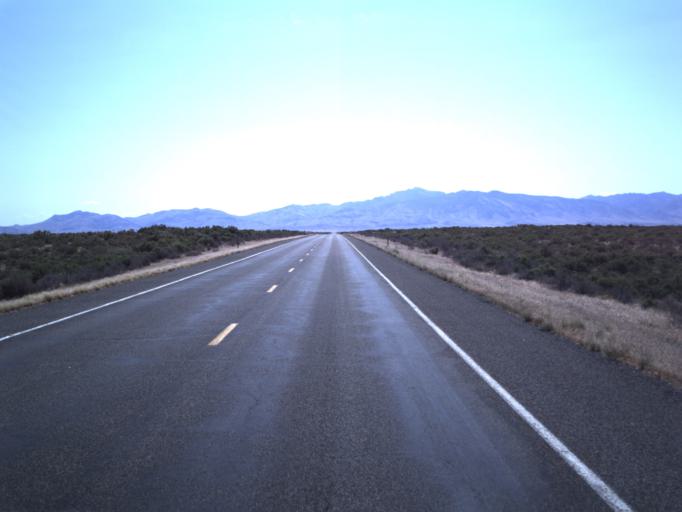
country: US
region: Utah
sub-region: Millard County
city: Delta
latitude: 39.4845
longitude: -112.5291
